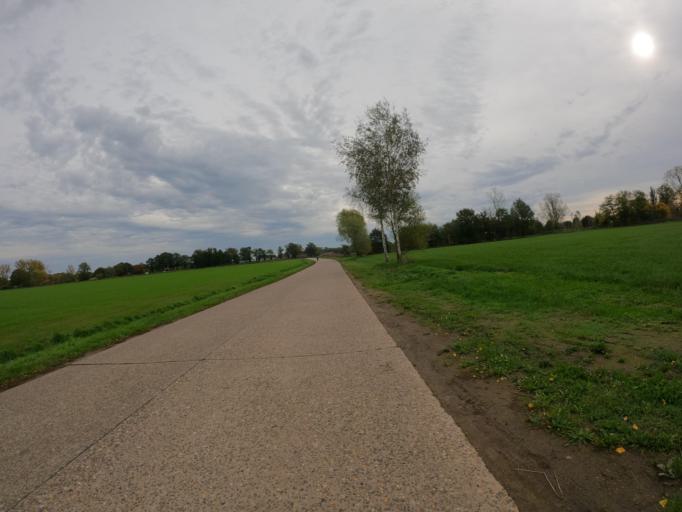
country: BE
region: Flanders
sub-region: Provincie Antwerpen
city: Hulshout
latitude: 51.0967
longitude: 4.8257
